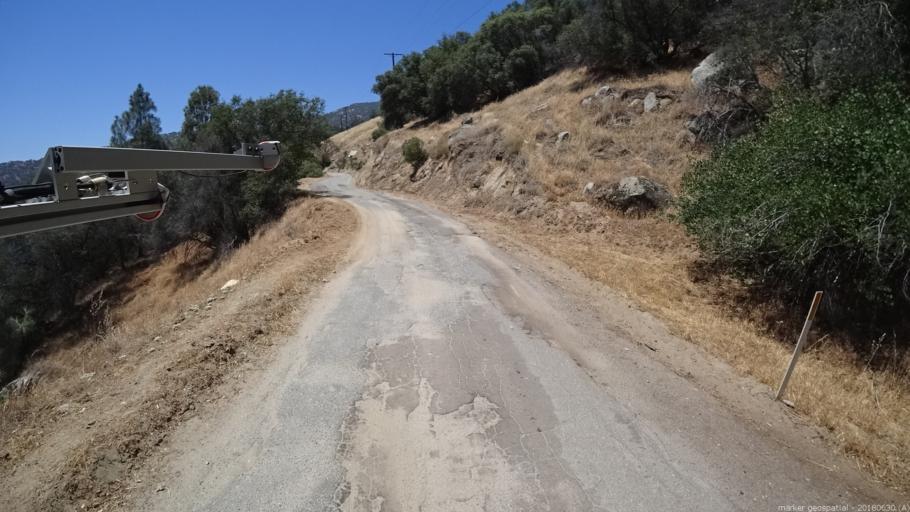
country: US
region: California
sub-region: Fresno County
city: Auberry
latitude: 37.1641
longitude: -119.4138
